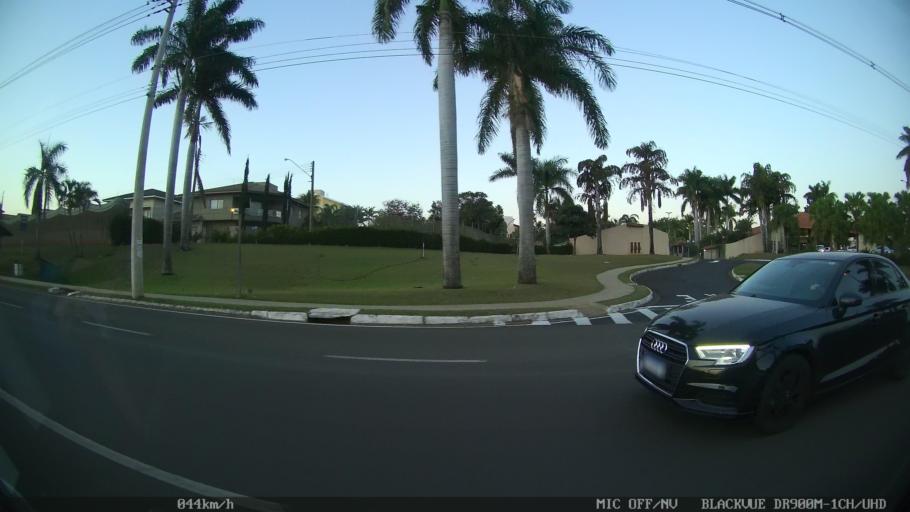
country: BR
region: Sao Paulo
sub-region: Sao Jose Do Rio Preto
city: Sao Jose do Rio Preto
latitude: -20.8205
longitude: -49.3452
